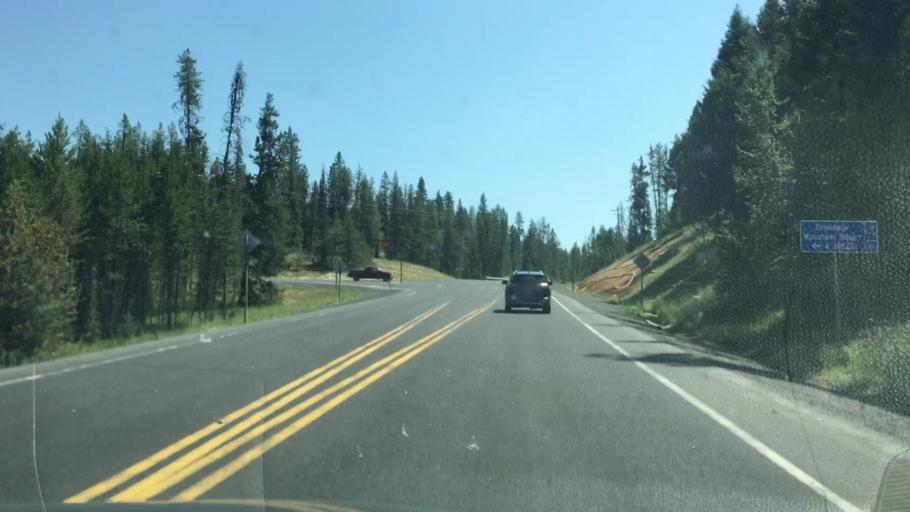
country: US
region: Idaho
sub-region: Valley County
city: McCall
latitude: 44.9588
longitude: -116.1713
